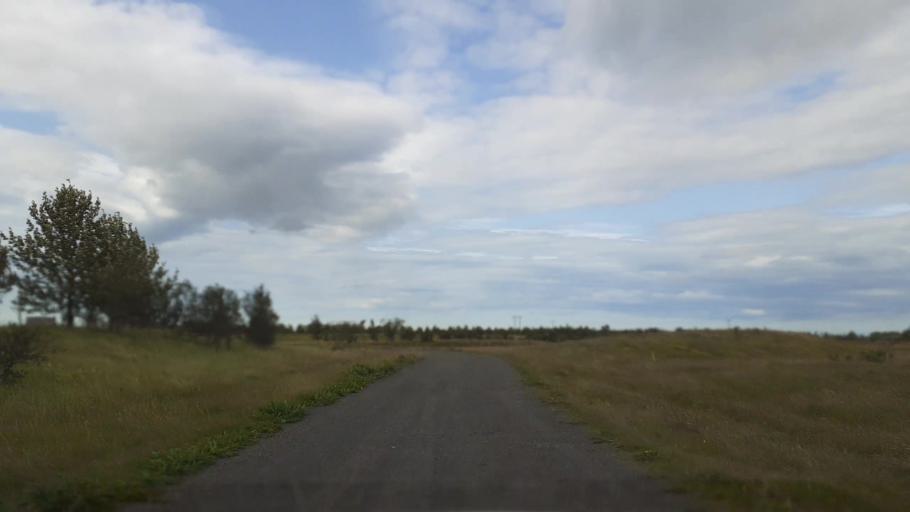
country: IS
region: South
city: Vestmannaeyjar
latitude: 63.7565
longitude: -20.2302
